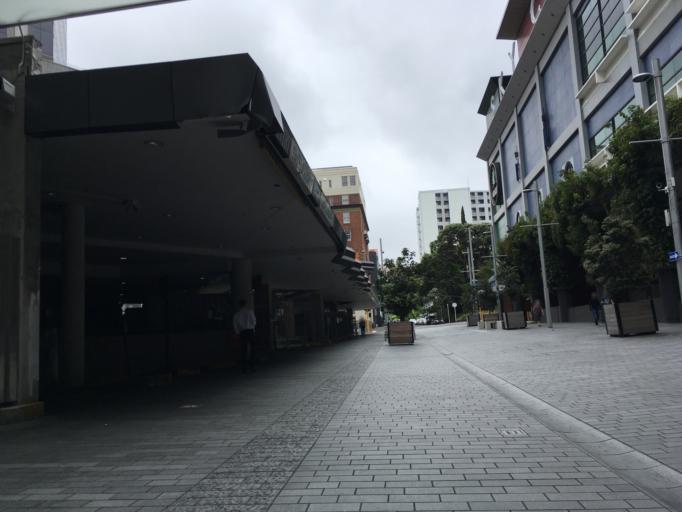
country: NZ
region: Auckland
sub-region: Auckland
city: Auckland
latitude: -36.8495
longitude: 174.7617
